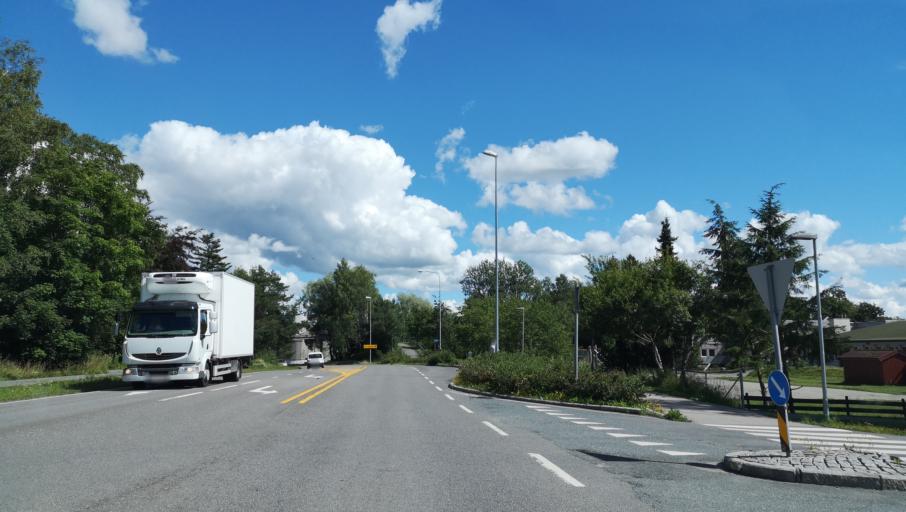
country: NO
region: Akershus
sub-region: As
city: As
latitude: 59.6642
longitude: 10.7850
